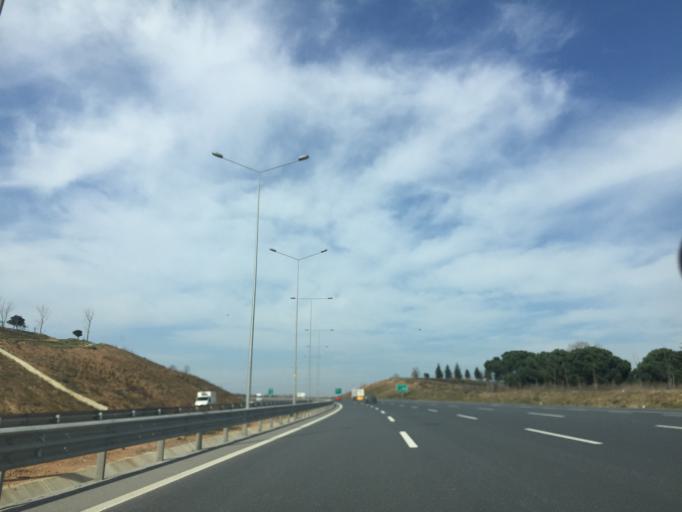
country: TR
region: Istanbul
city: Sultanbeyli
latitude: 40.9835
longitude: 29.3288
